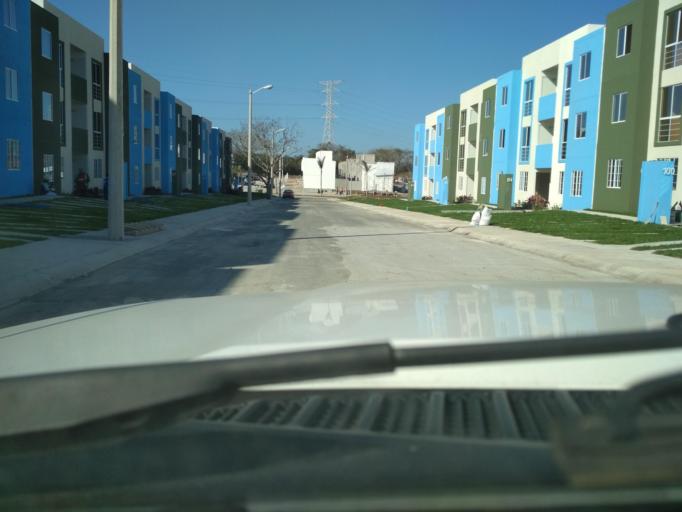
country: MX
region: Veracruz
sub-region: Veracruz
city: Las Amapolas
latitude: 19.1439
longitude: -96.2337
